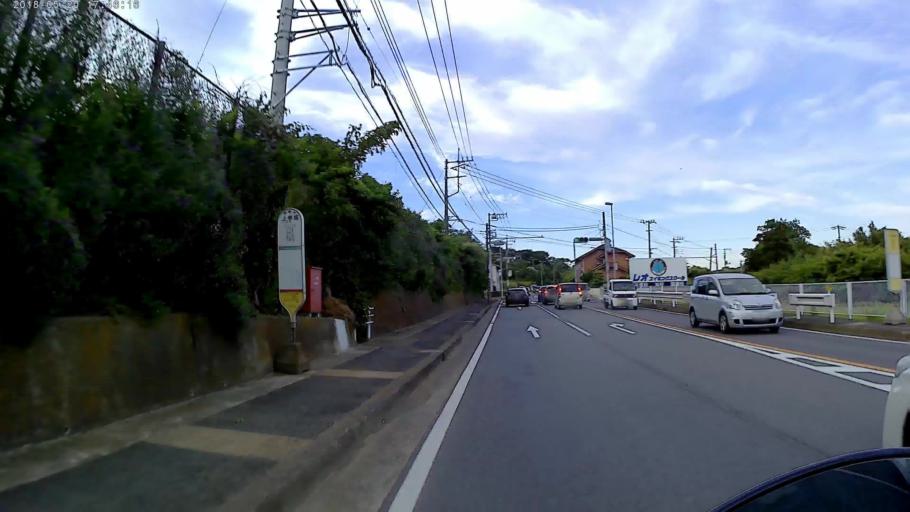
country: JP
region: Kanagawa
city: Oiso
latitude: 35.3272
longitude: 139.2898
